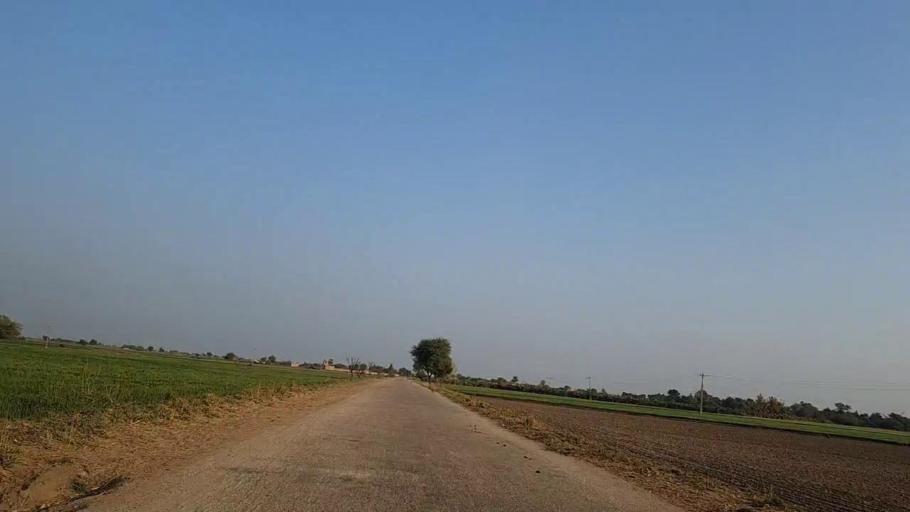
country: PK
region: Sindh
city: Sakrand
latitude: 26.0423
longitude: 68.4259
